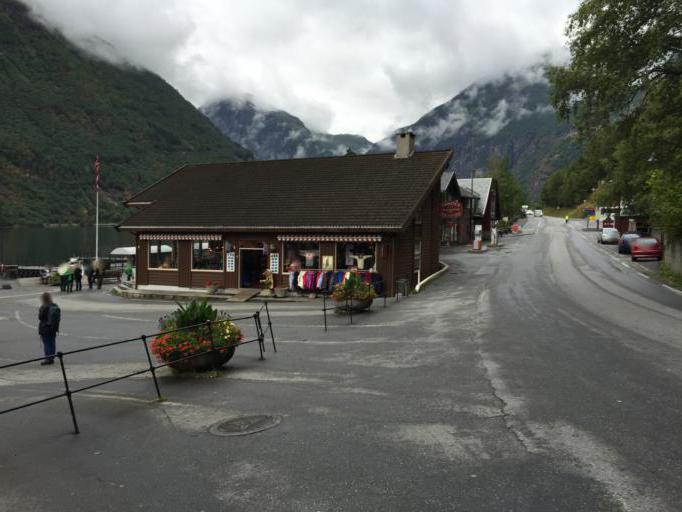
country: NO
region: More og Romsdal
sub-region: Norddal
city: Valldal
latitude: 62.1023
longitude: 7.2059
